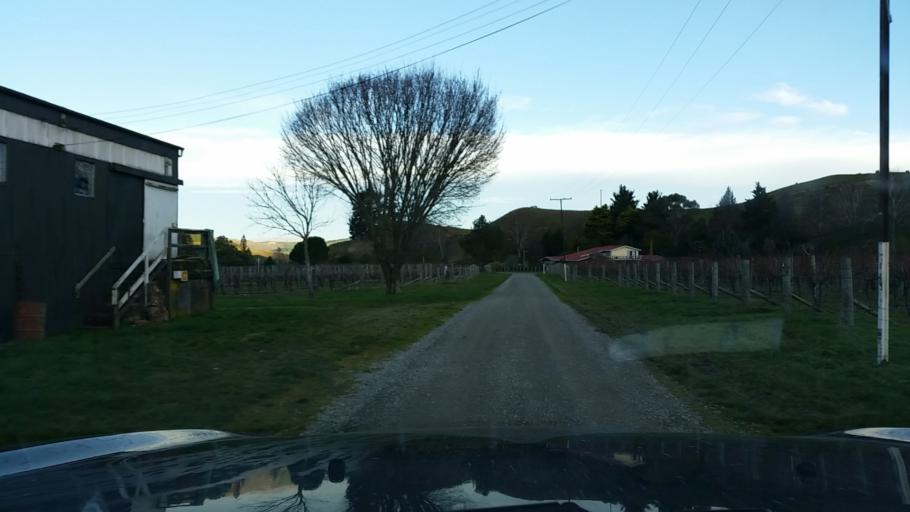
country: NZ
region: Nelson
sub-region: Nelson City
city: Nelson
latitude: -41.5049
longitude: 173.5767
